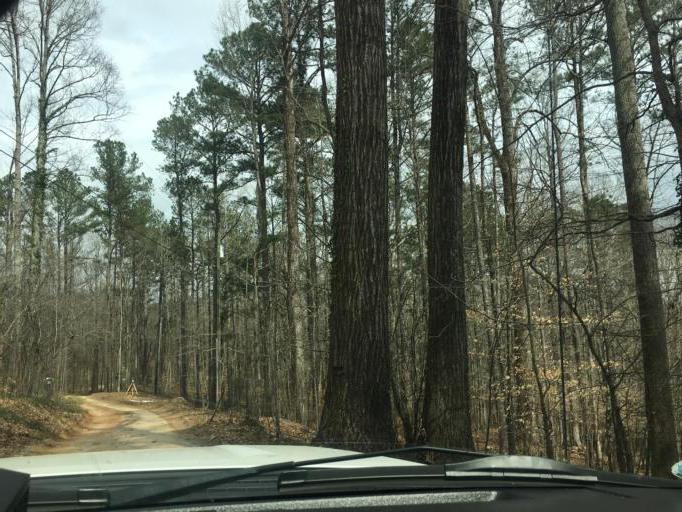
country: US
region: Georgia
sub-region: Fulton County
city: Milton
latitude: 34.2073
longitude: -84.3144
